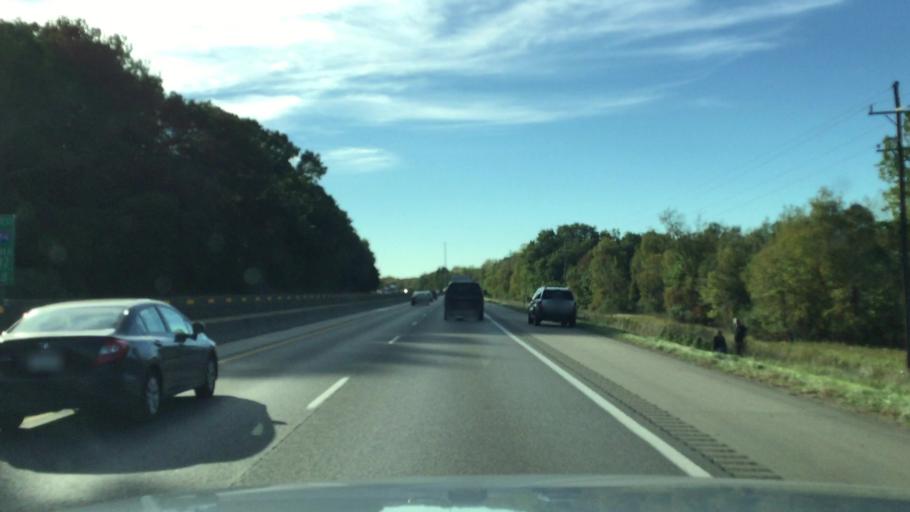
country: US
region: Michigan
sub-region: Kalamazoo County
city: Galesburg
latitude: 42.2705
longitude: -85.4727
